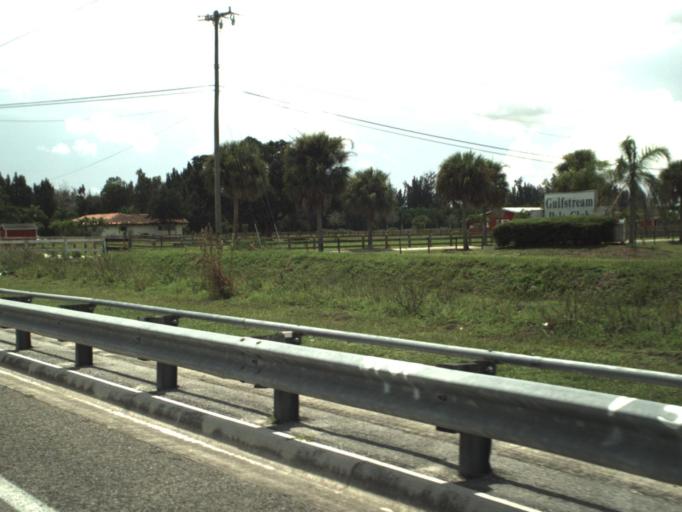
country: US
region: Florida
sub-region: Palm Beach County
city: Greenacres City
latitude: 26.6172
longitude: -80.1822
